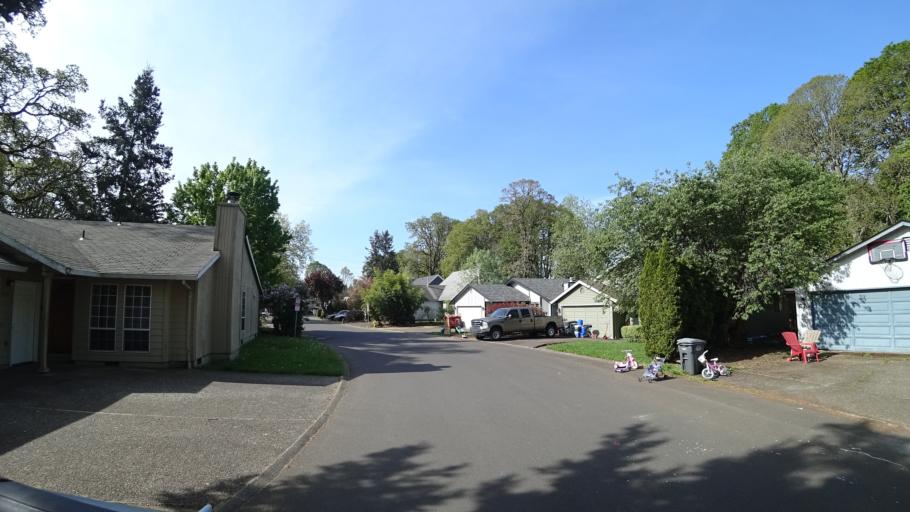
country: US
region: Oregon
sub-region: Washington County
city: Hillsboro
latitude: 45.5250
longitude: -122.9580
